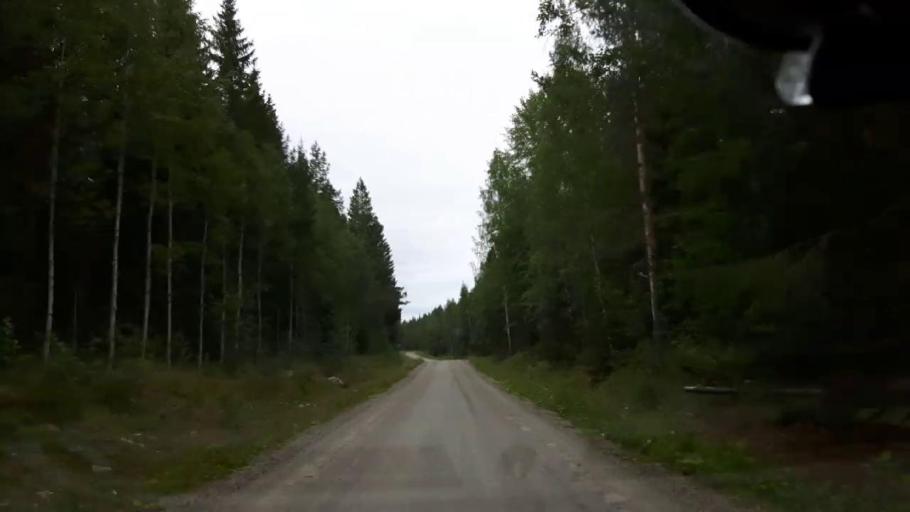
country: SE
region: Jaemtland
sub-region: Braecke Kommun
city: Braecke
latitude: 62.8245
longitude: 15.7111
